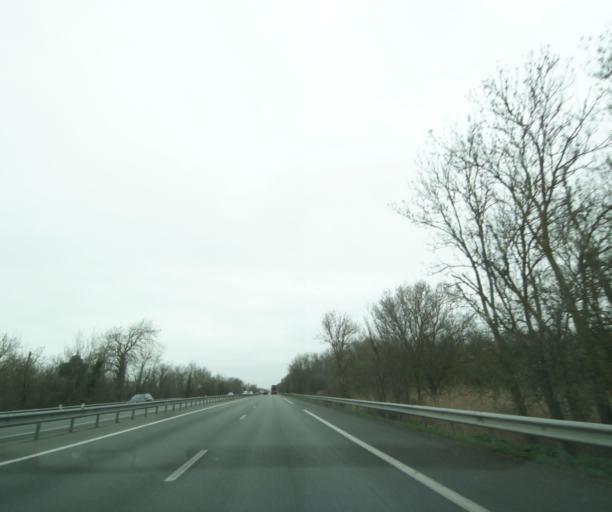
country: FR
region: Poitou-Charentes
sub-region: Departement de la Charente-Maritime
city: Chatelaillon-Plage
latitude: 46.0936
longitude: -1.0869
